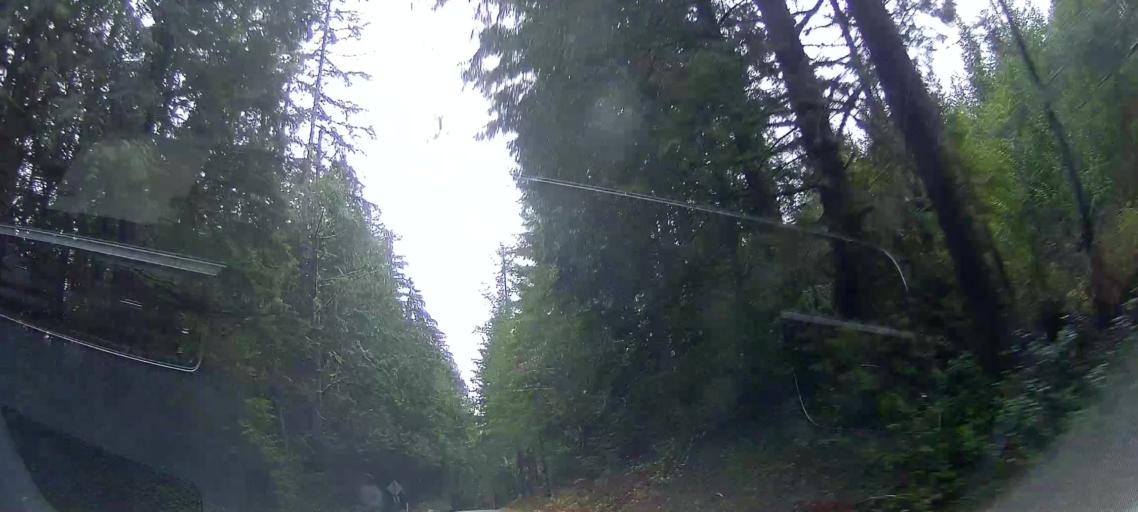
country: US
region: Washington
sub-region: Snohomish County
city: Darrington
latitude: 48.5292
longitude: -121.3933
